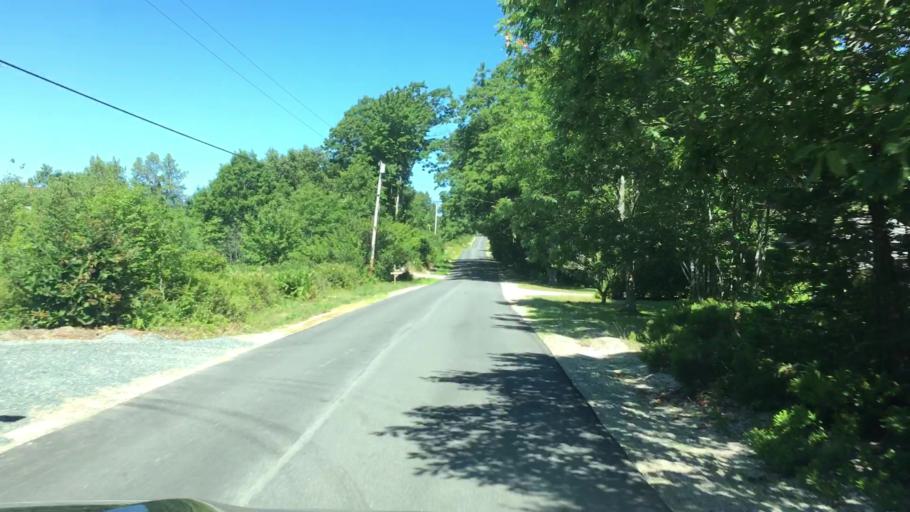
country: US
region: Maine
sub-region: Hancock County
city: Sedgwick
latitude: 44.3205
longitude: -68.6300
